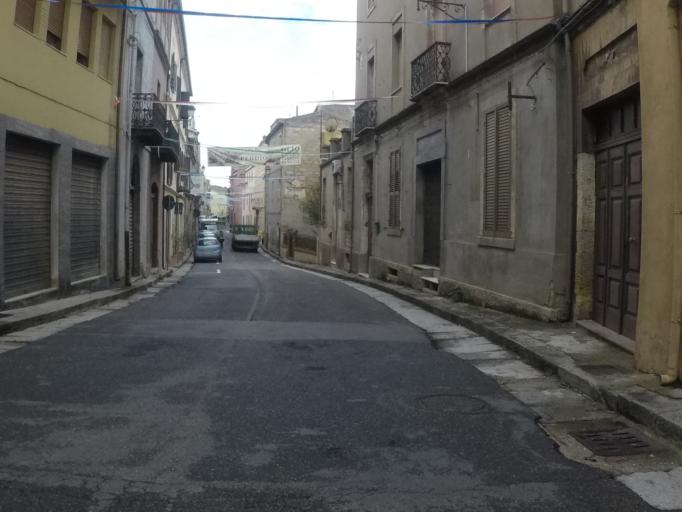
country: IT
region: Sardinia
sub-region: Provincia di Oristano
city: Cuglieri
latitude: 40.1904
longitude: 8.5682
